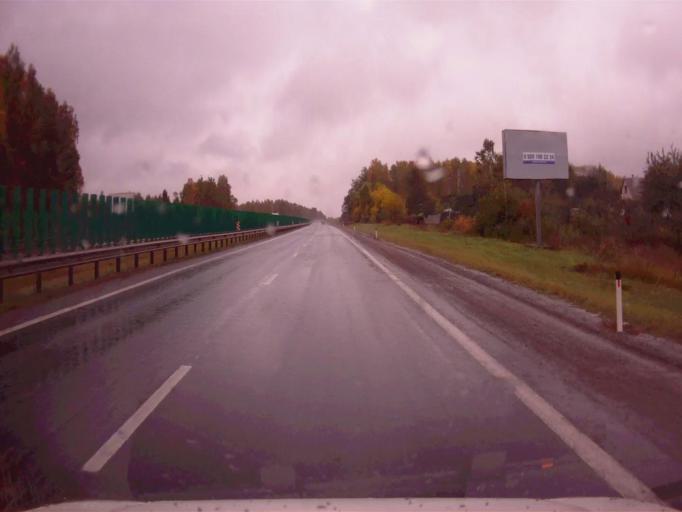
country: RU
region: Chelyabinsk
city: Dolgoderevenskoye
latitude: 55.3304
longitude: 61.3210
